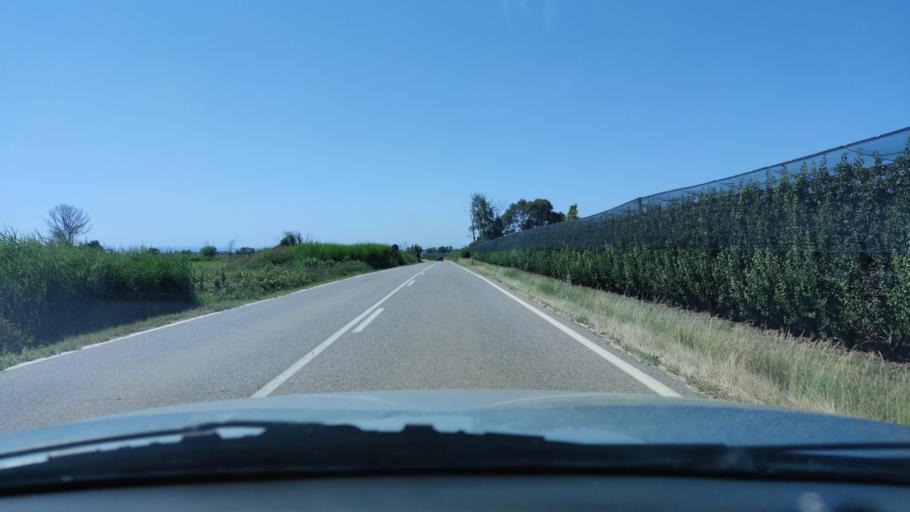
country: ES
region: Catalonia
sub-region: Provincia de Lleida
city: Penelles
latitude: 41.7277
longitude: 0.9827
